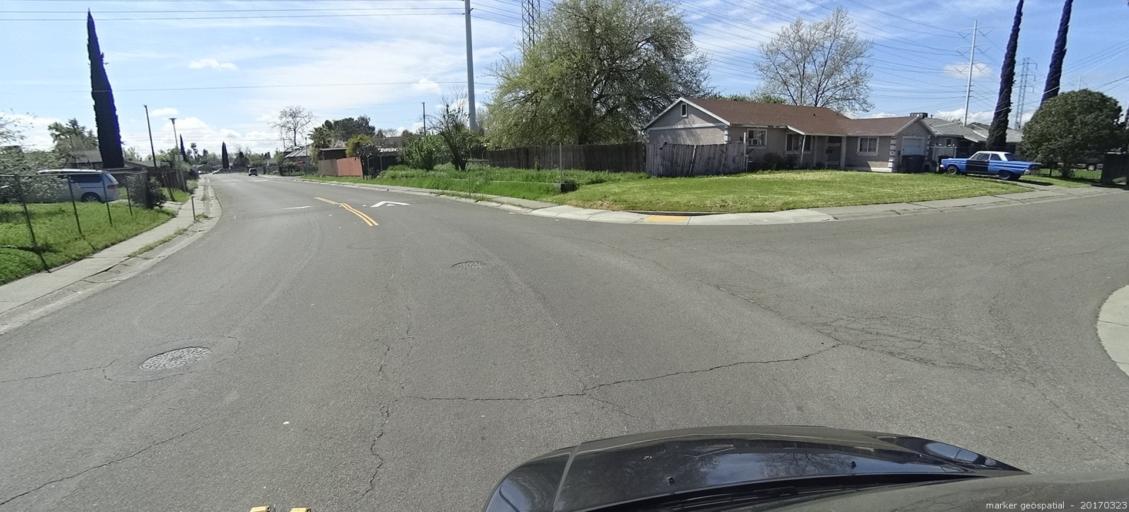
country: US
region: California
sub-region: Sacramento County
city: Florin
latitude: 38.5092
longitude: -121.4134
